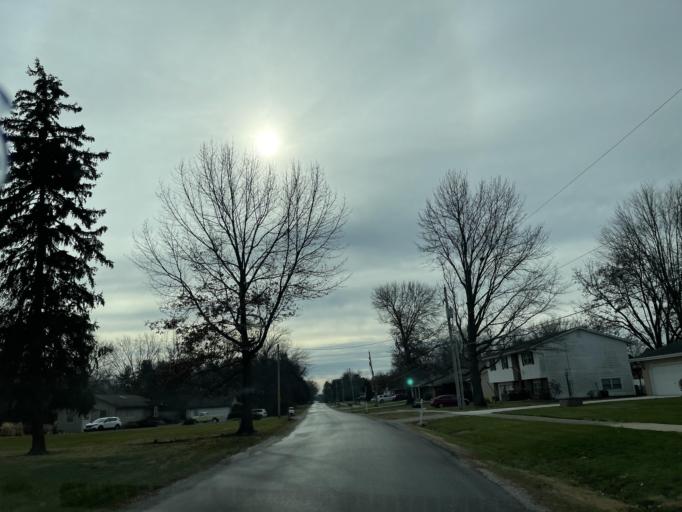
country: US
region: Illinois
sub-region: Sangamon County
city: Leland Grove
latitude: 39.8049
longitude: -89.7298
